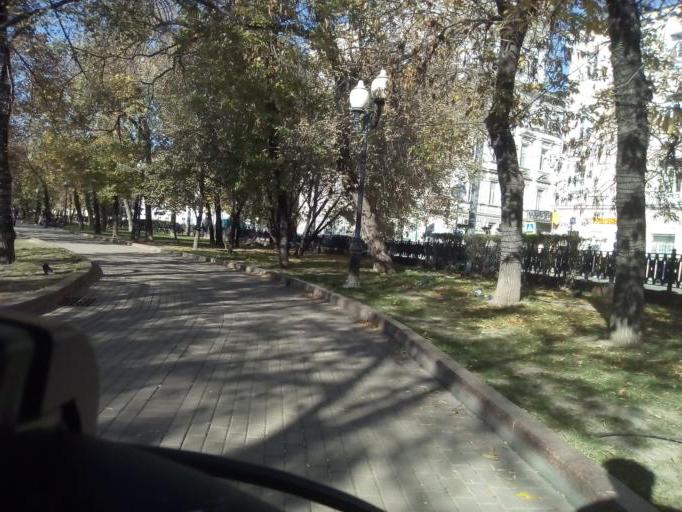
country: RU
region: Moscow
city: Zamoskvorech'ye
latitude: 55.7604
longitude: 37.6459
